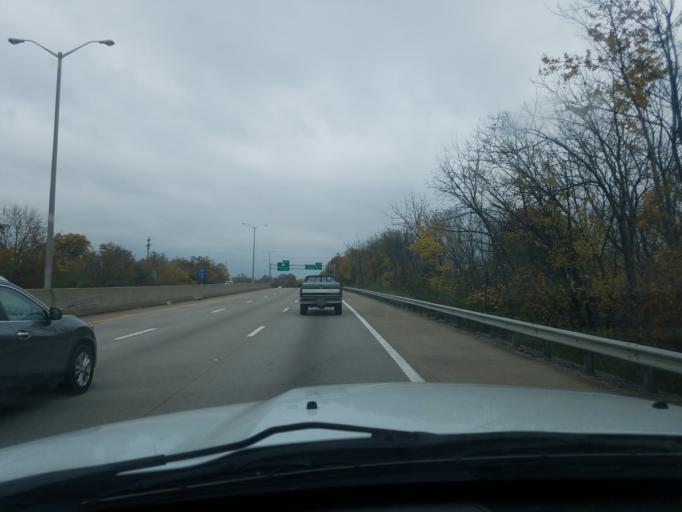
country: US
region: Indiana
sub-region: Floyd County
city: New Albany
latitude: 38.2447
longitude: -85.8126
